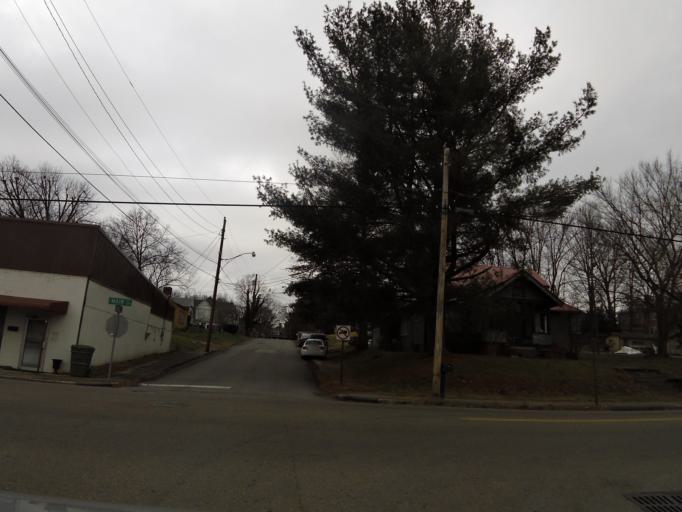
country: US
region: Tennessee
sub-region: Hamblen County
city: Morristown
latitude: 36.2154
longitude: -83.2883
